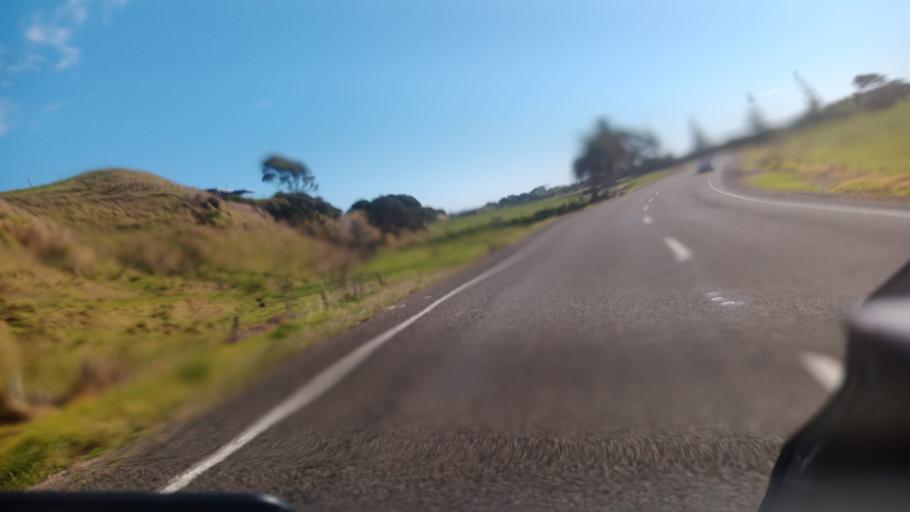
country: NZ
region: Bay of Plenty
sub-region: Opotiki District
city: Opotiki
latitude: -37.9919
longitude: 177.3182
